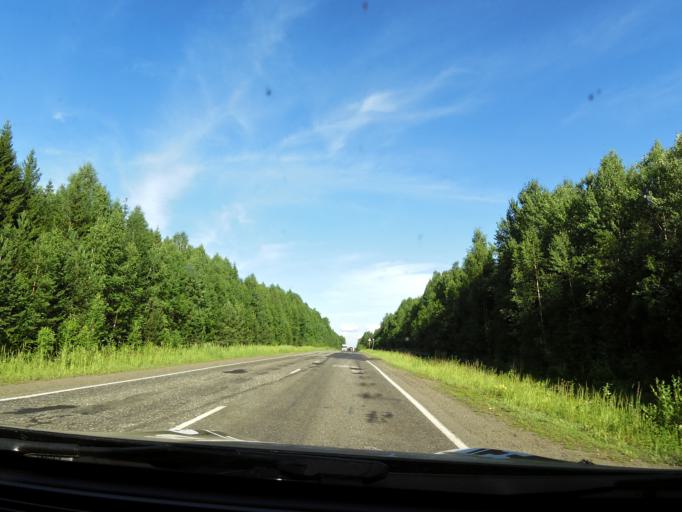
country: RU
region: Kirov
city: Chernaya Kholunitsa
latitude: 58.8790
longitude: 51.4523
